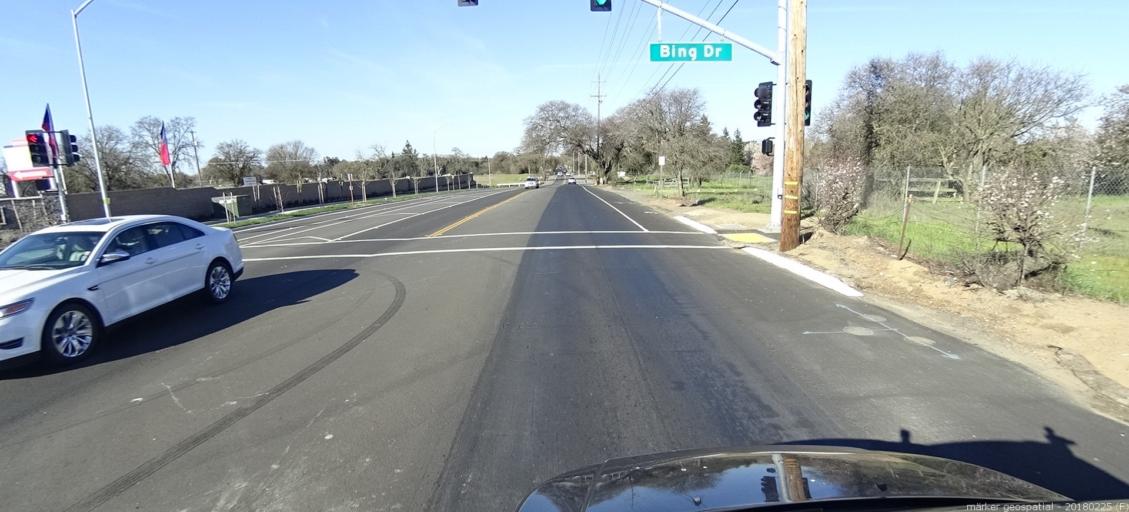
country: US
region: California
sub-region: Sacramento County
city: North Highlands
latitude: 38.7143
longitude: -121.3972
